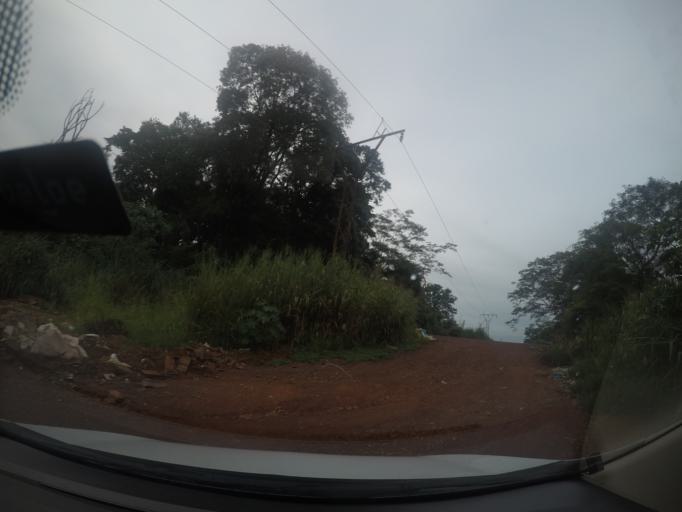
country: BR
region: Goias
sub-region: Goiania
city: Goiania
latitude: -16.6324
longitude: -49.2403
